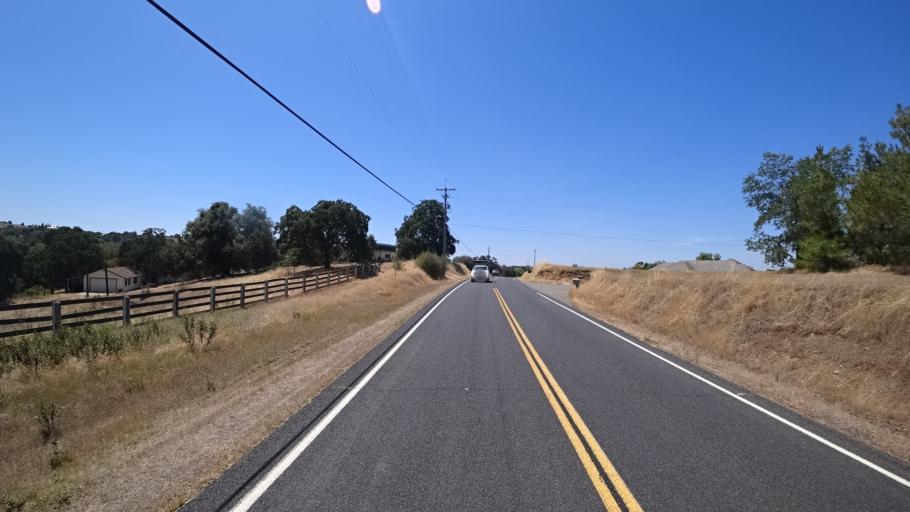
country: US
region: California
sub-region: Calaveras County
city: Rancho Calaveras
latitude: 38.1560
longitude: -120.9434
